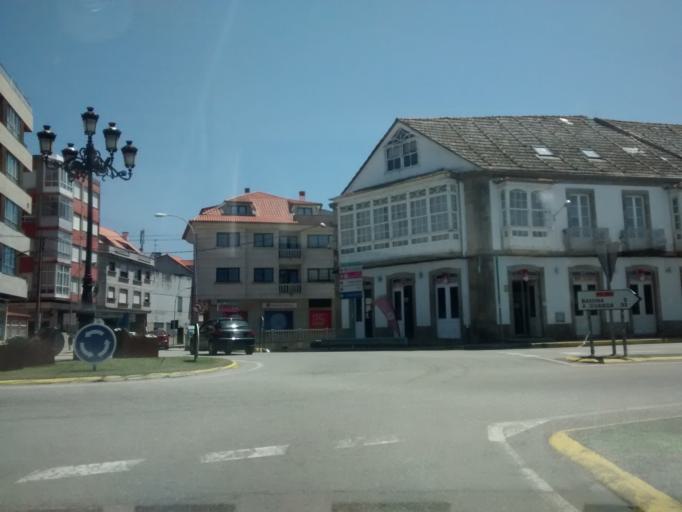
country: ES
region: Galicia
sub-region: Provincia de Pontevedra
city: Nigran
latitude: 42.1164
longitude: -8.8129
